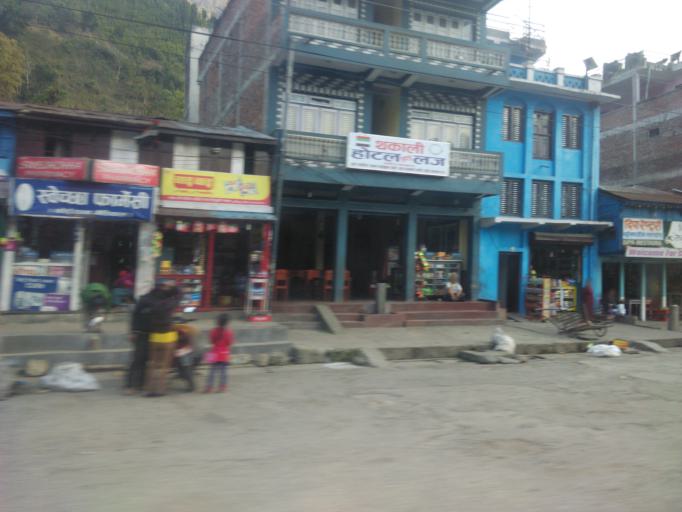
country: NP
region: Central Region
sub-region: Narayani Zone
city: Bharatpur
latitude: 27.8571
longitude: 84.5630
